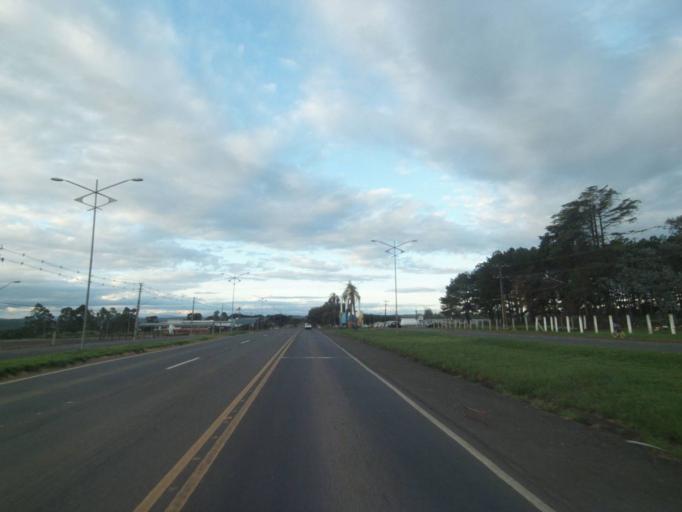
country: BR
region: Parana
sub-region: Telemaco Borba
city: Telemaco Borba
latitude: -24.3408
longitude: -50.6570
